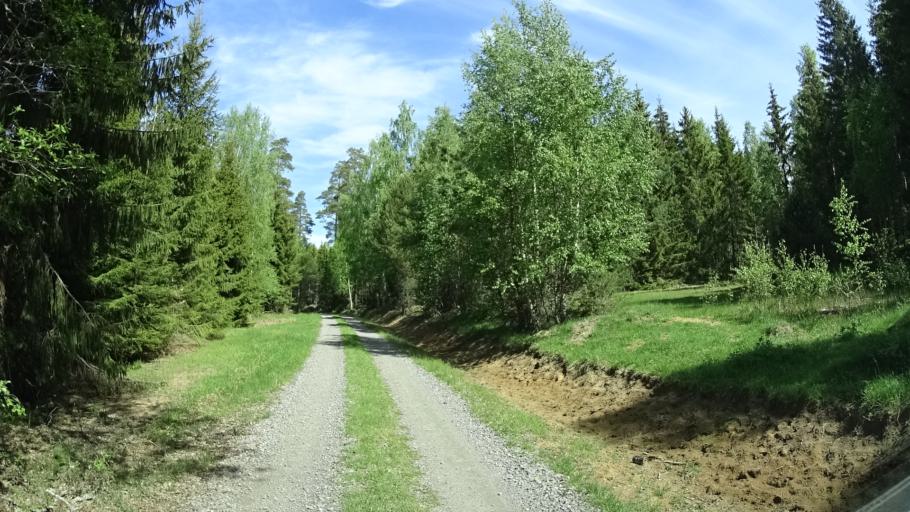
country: SE
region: OEstergoetland
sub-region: Finspangs Kommun
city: Finspang
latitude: 58.8047
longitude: 15.8405
